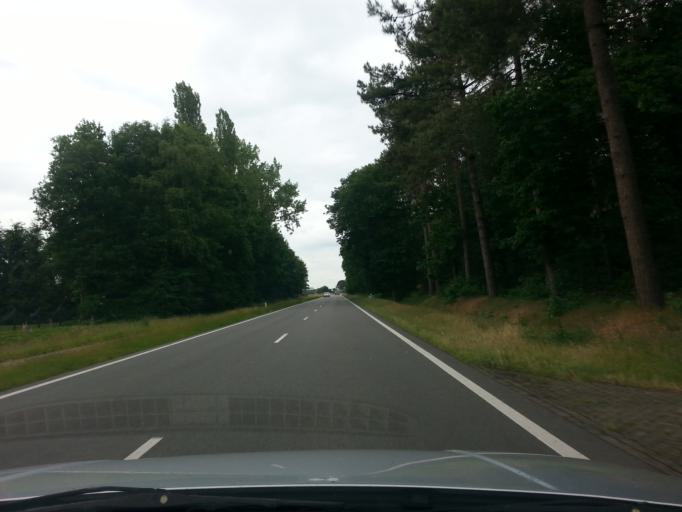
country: NL
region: North Brabant
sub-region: Gemeente Boxmeer
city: Overloon
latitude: 51.5140
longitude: 5.8857
